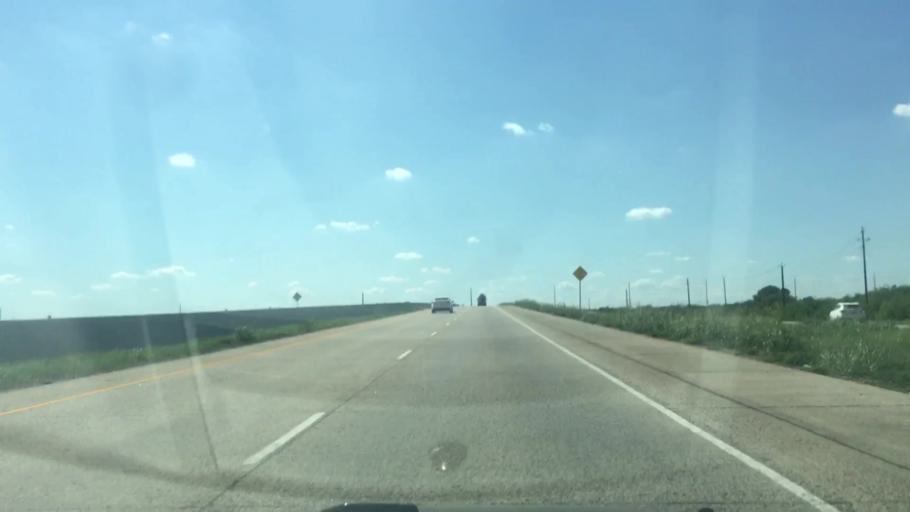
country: US
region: Texas
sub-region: Denton County
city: Denton
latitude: 33.2604
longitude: -97.1279
